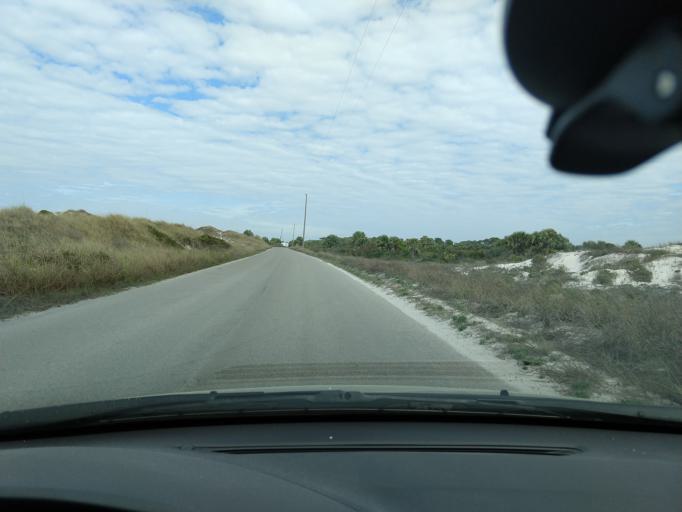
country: US
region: Florida
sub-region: Gulf County
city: Port Saint Joe
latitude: 29.7690
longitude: -85.4051
